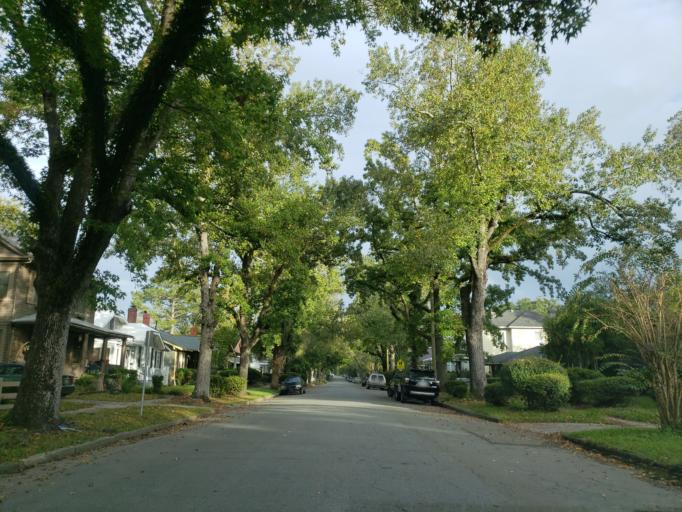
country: US
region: Georgia
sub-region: Chatham County
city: Savannah
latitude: 32.0620
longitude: -81.0864
